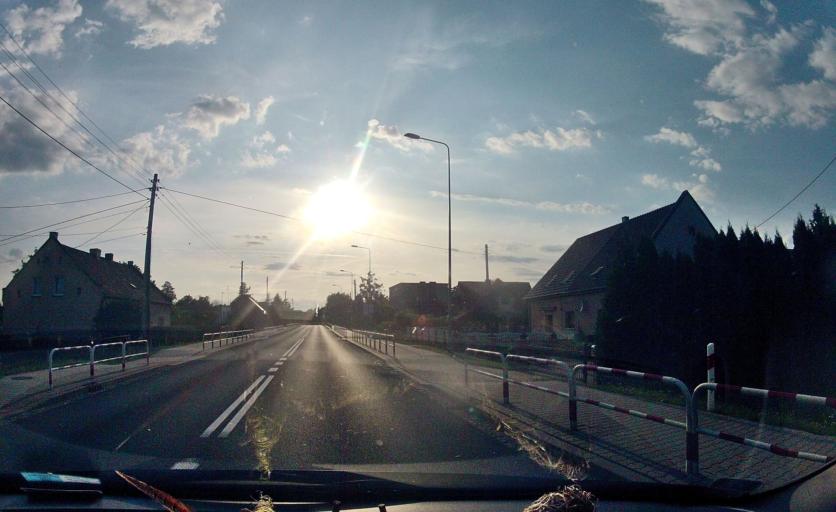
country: PL
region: Opole Voivodeship
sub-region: Powiat kluczborski
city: Kluczbork
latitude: 50.9748
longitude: 18.2326
